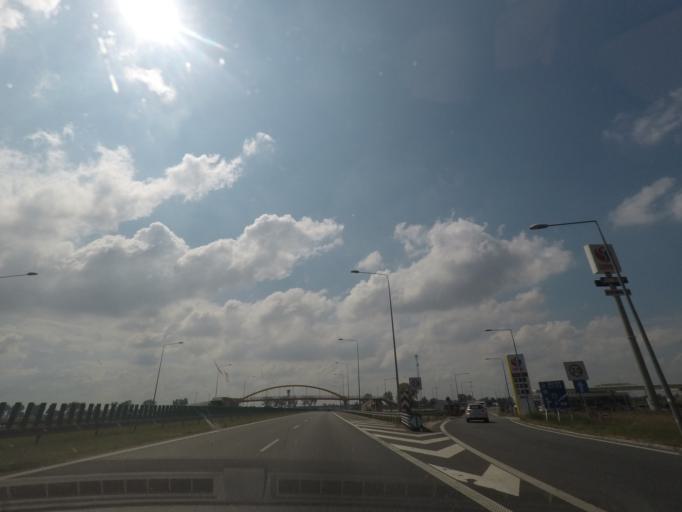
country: PL
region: Lodz Voivodeship
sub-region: Powiat kutnowski
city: Krzyzanow
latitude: 52.1878
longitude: 19.4873
